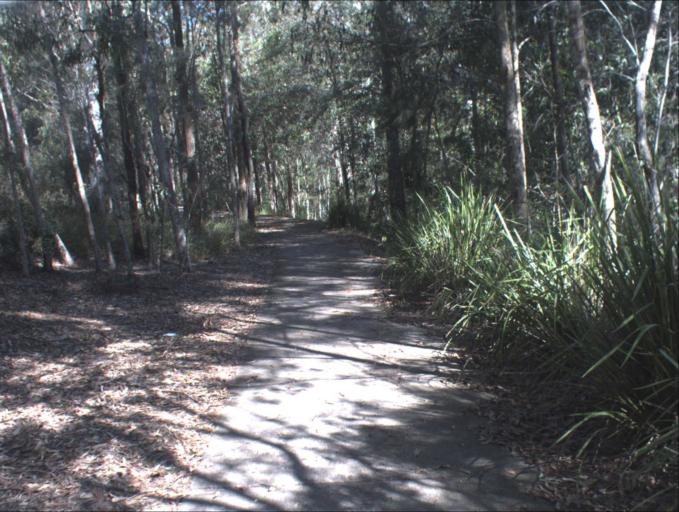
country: AU
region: Queensland
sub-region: Logan
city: Waterford West
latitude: -27.7130
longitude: 153.1515
